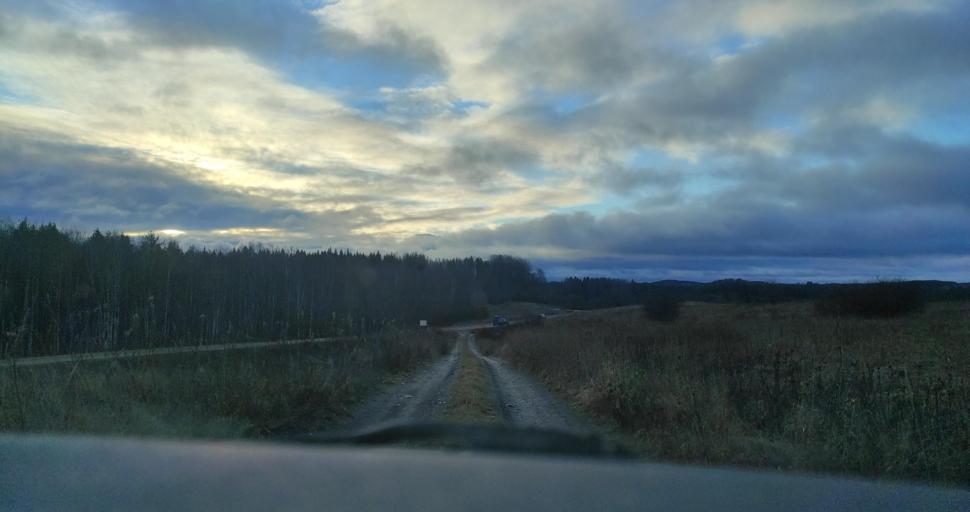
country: RU
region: Republic of Karelia
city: Pitkyaranta
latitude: 61.7270
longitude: 31.3836
